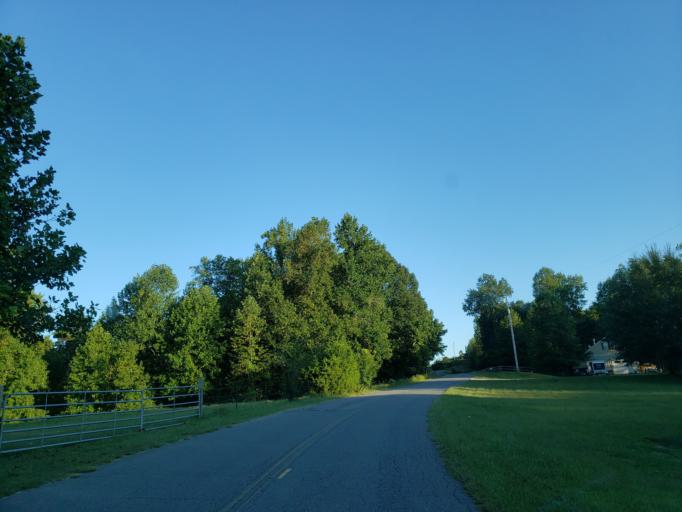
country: US
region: Georgia
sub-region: Bartow County
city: Rydal
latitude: 34.3959
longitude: -84.6700
